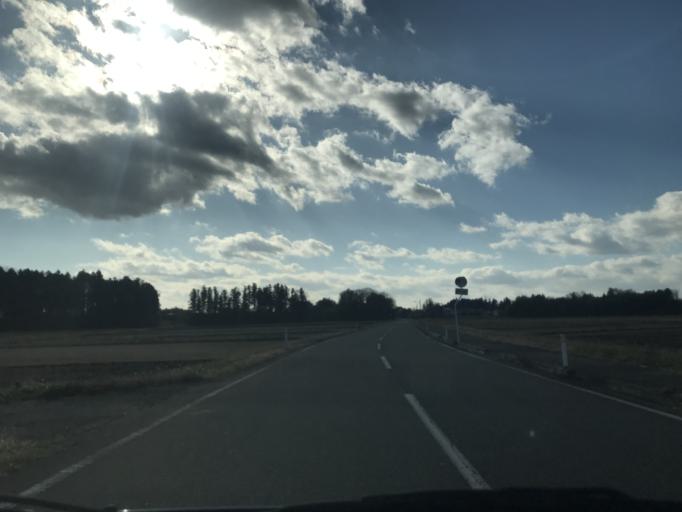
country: JP
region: Iwate
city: Ichinoseki
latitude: 38.7653
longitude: 141.0596
